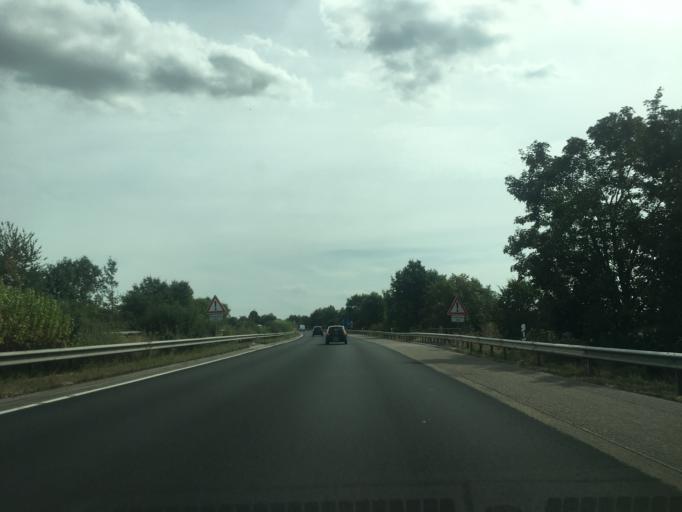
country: DE
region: Rheinland-Pfalz
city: Saffig
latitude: 50.3671
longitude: 7.4220
